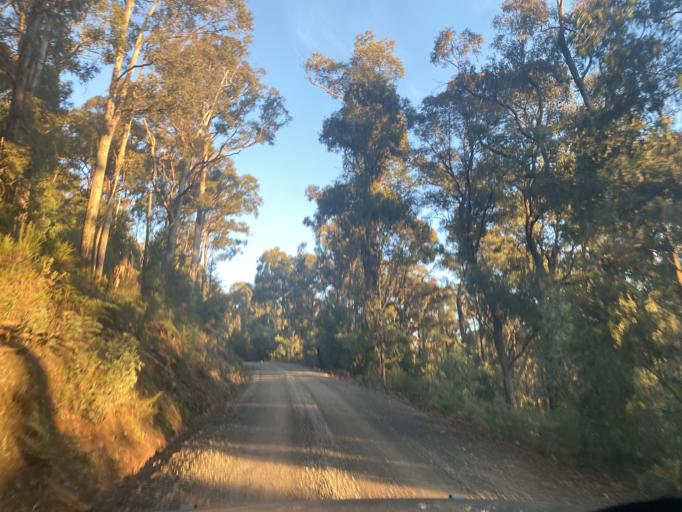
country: AU
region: Victoria
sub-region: Yarra Ranges
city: Healesville
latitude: -37.4253
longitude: 145.5283
